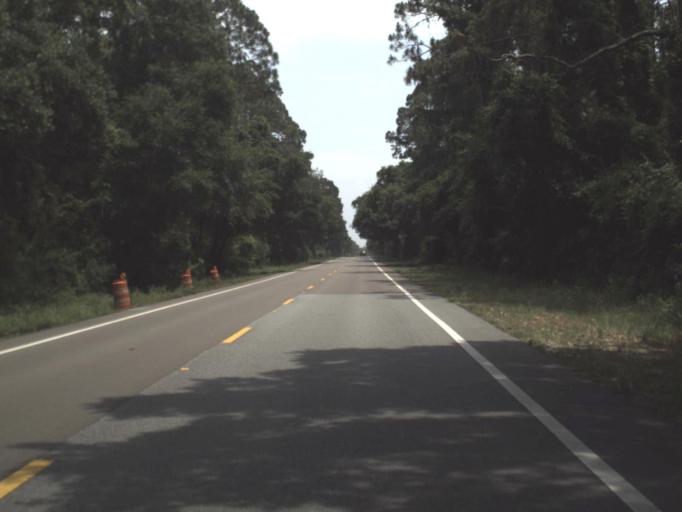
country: US
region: Florida
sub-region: Nassau County
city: Fernandina Beach
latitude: 30.5038
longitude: -81.4541
